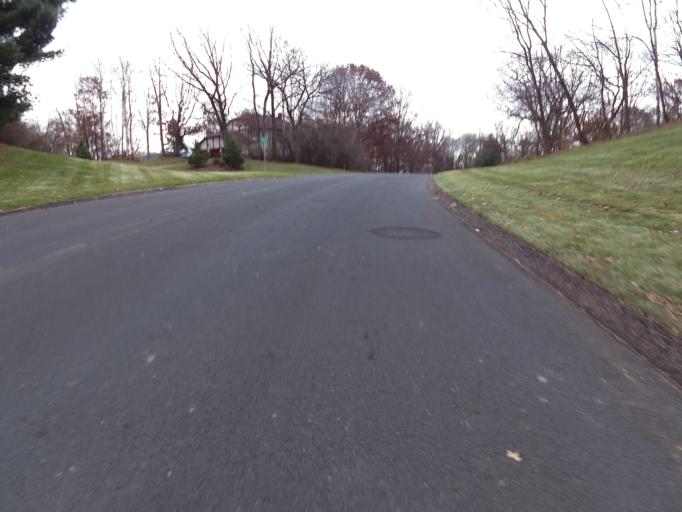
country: US
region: Minnesota
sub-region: Washington County
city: Lake Elmo
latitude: 44.9841
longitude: -92.8713
